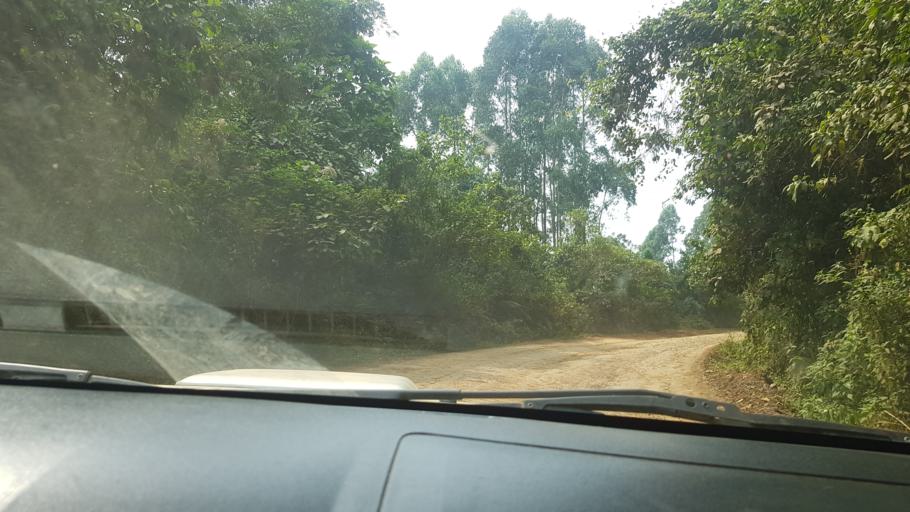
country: ET
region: Oromiya
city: Gore
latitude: 7.8191
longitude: 35.4601
